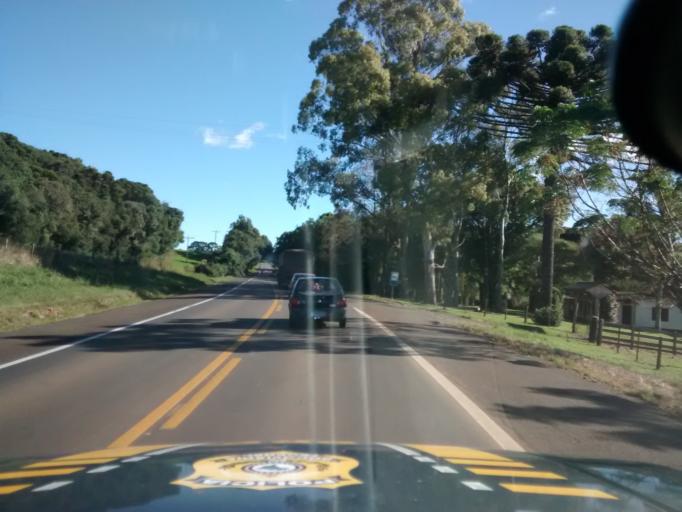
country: BR
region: Rio Grande do Sul
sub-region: Lagoa Vermelha
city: Lagoa Vermelha
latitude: -28.2945
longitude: -51.4453
